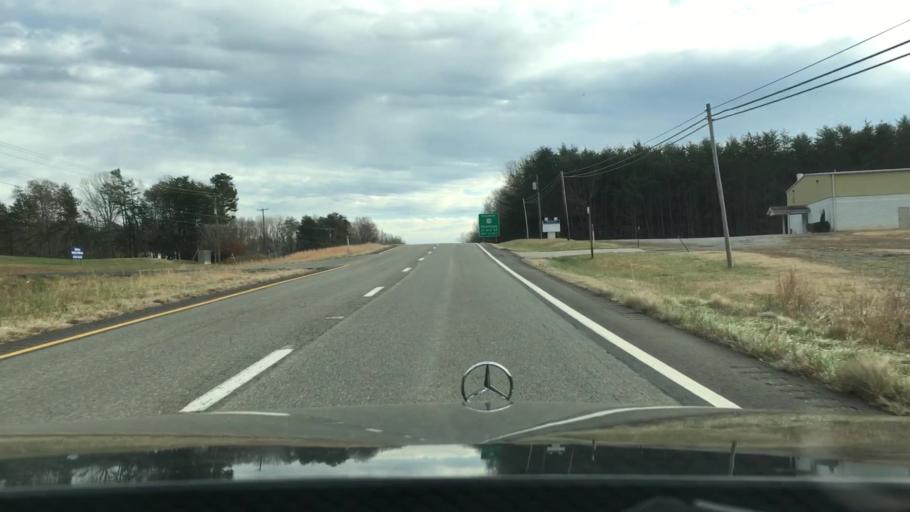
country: US
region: Virginia
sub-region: Pittsylvania County
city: Chatham
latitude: 36.8575
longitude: -79.3986
